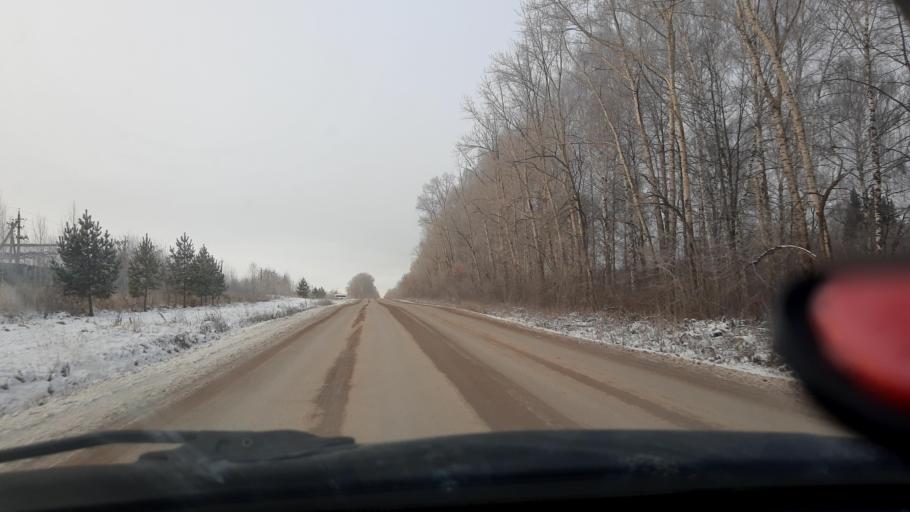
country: RU
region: Bashkortostan
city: Iglino
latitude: 54.8366
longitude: 56.4471
